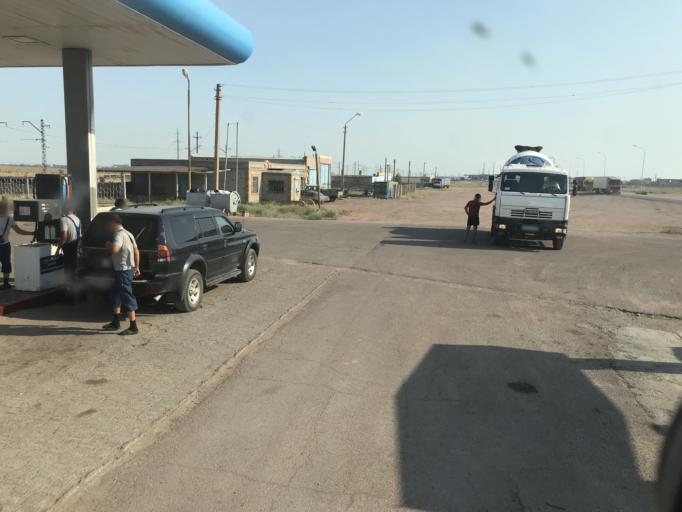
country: KZ
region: Qaraghandy
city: Balqash
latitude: 46.8765
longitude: 74.9503
